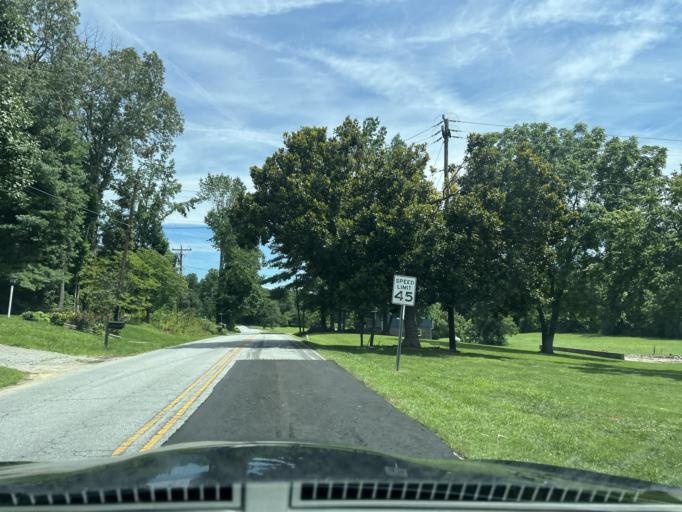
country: US
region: North Carolina
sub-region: Henderson County
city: Fruitland
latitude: 35.3954
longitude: -82.3912
